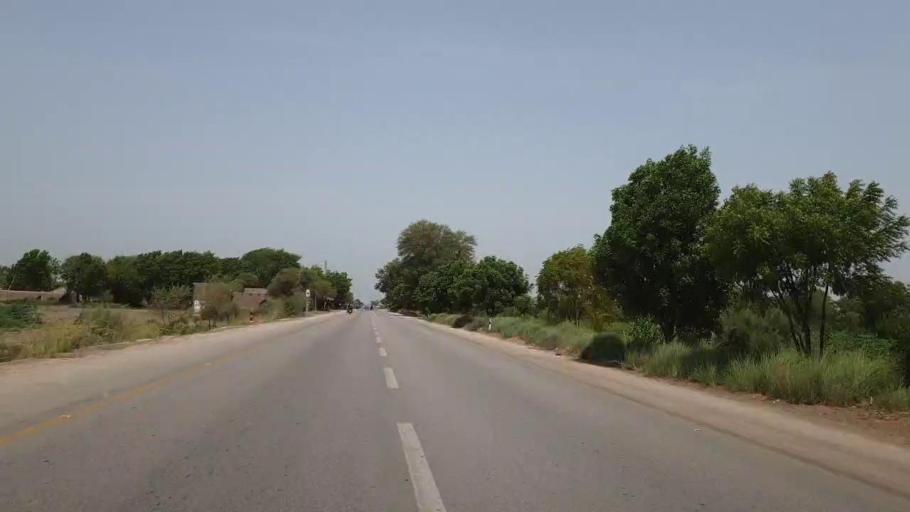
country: PK
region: Sindh
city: Nawabshah
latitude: 26.2207
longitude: 68.4999
